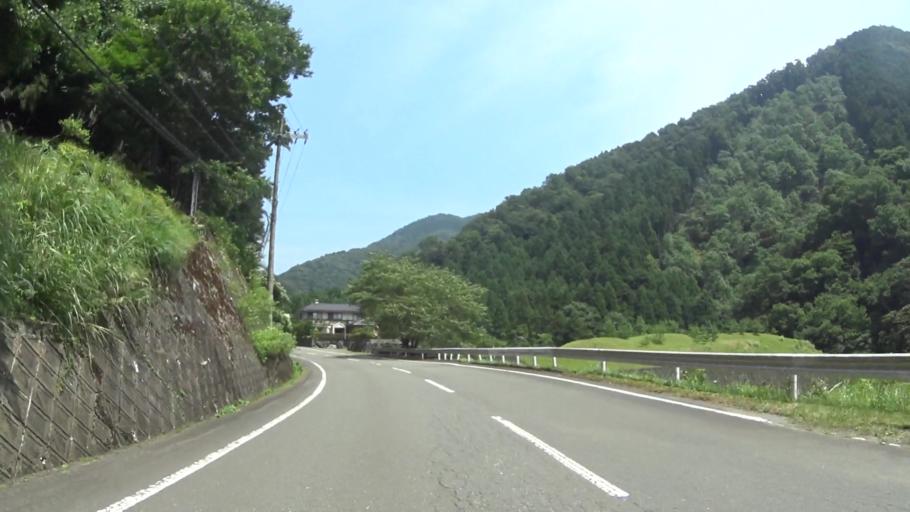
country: JP
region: Kyoto
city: Ayabe
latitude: 35.2899
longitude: 135.4264
